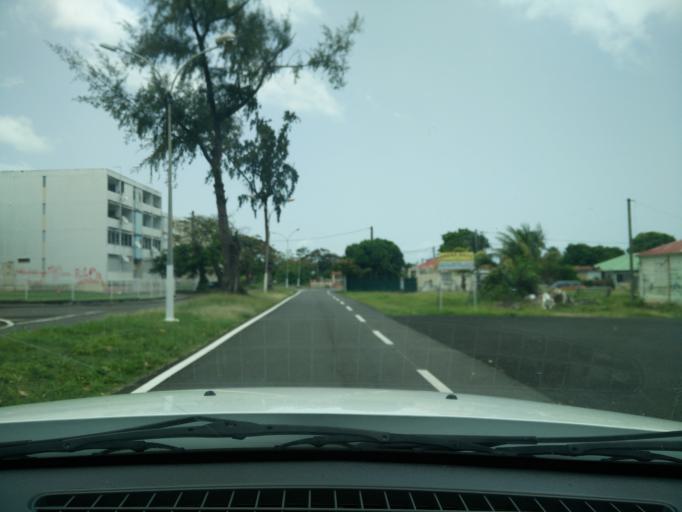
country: GP
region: Guadeloupe
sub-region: Guadeloupe
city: Capesterre-Belle-Eau
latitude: 16.0528
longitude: -61.5621
